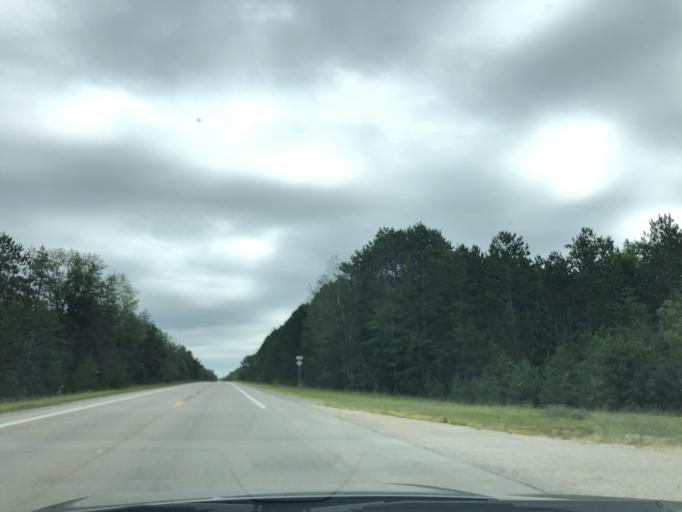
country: US
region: Michigan
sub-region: Clare County
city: Harrison
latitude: 44.0313
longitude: -85.0085
